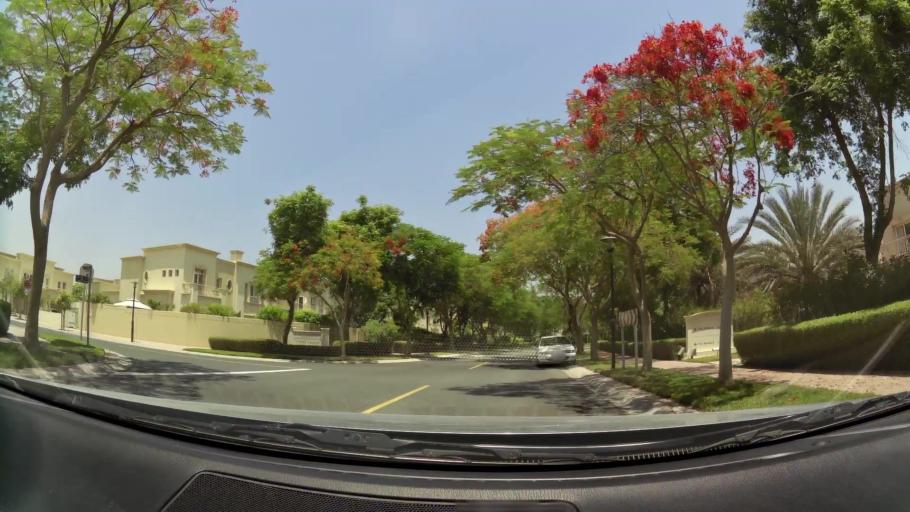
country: AE
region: Dubai
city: Dubai
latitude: 25.0581
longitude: 55.1876
